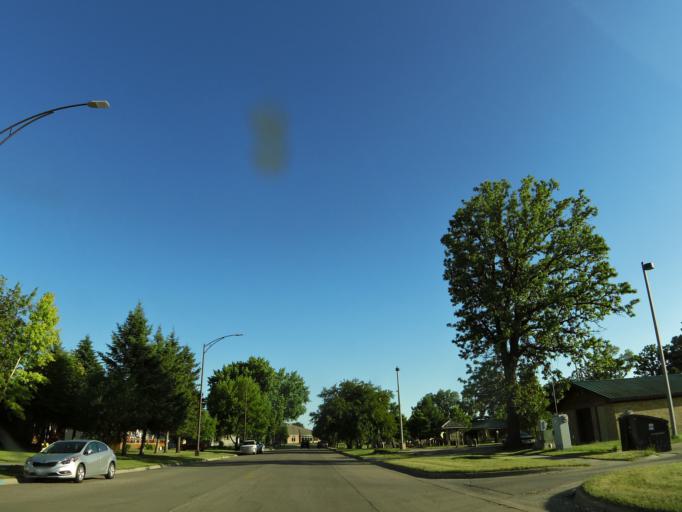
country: US
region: Minnesota
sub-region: Polk County
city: East Grand Forks
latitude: 47.9335
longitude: -97.0256
